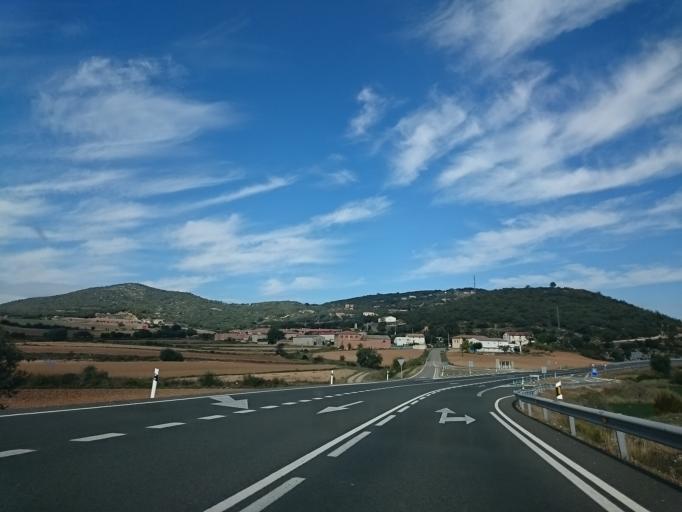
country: ES
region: Aragon
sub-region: Provincia de Huesca
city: Benavarri / Benabarre
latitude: 42.0451
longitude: 0.4636
